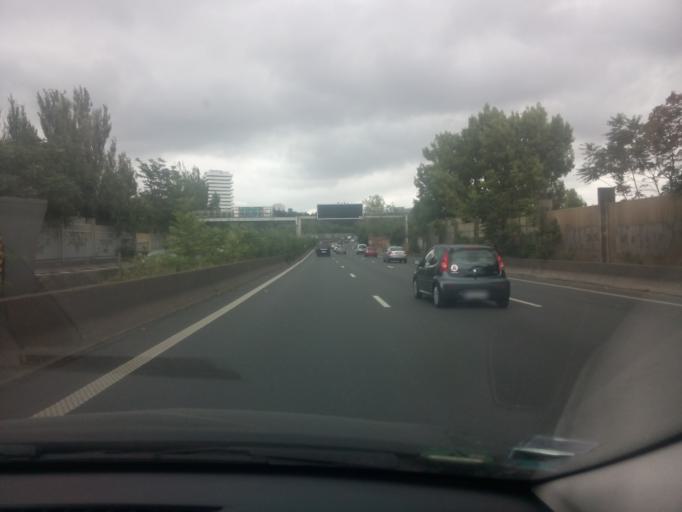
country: FR
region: Ile-de-France
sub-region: Departement du Val-de-Marne
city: Gentilly
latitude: 48.8091
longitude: 2.3392
